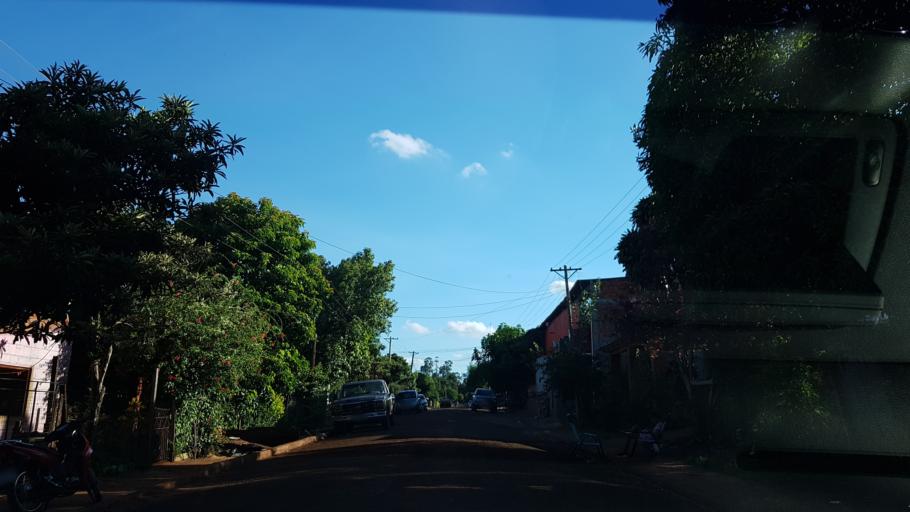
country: AR
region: Misiones
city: Puerto Libertad
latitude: -25.9153
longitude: -54.5886
